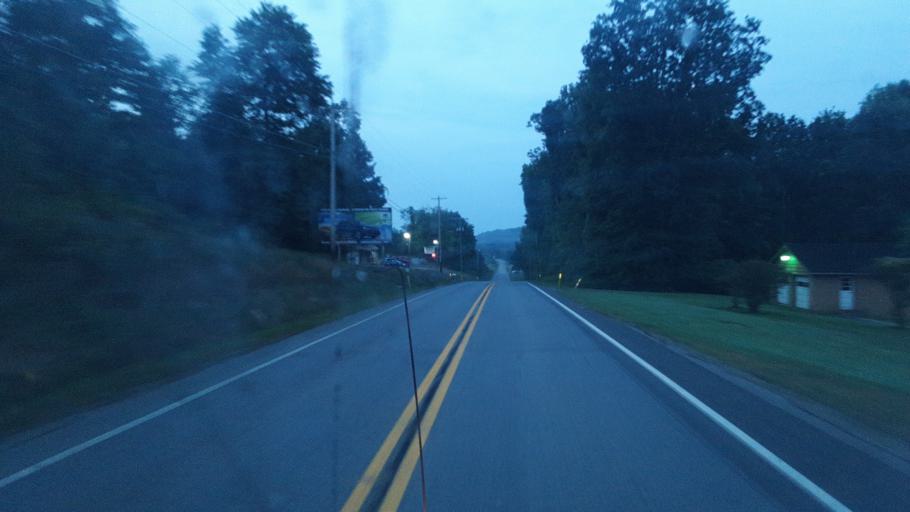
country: US
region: Pennsylvania
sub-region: Clarion County
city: Clarion
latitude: 41.0724
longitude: -79.3191
